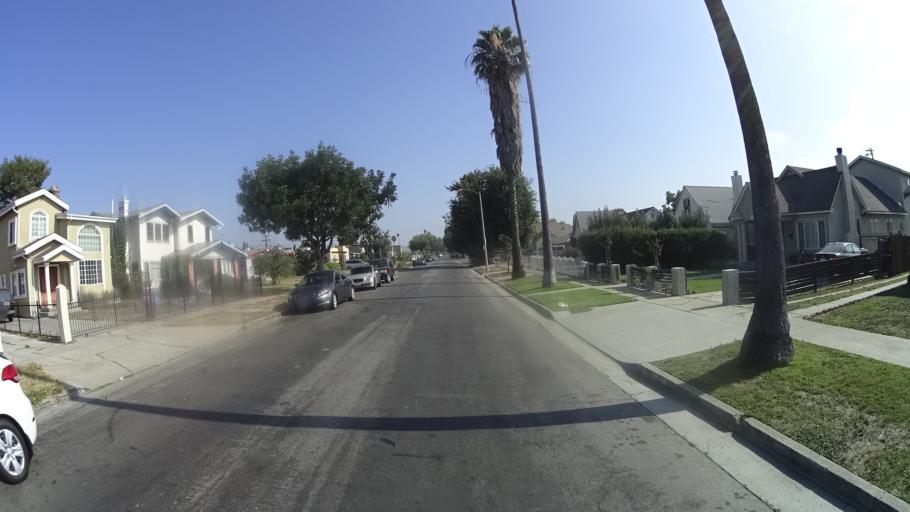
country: US
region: California
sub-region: Los Angeles County
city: View Park-Windsor Hills
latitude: 33.9894
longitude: -118.3322
